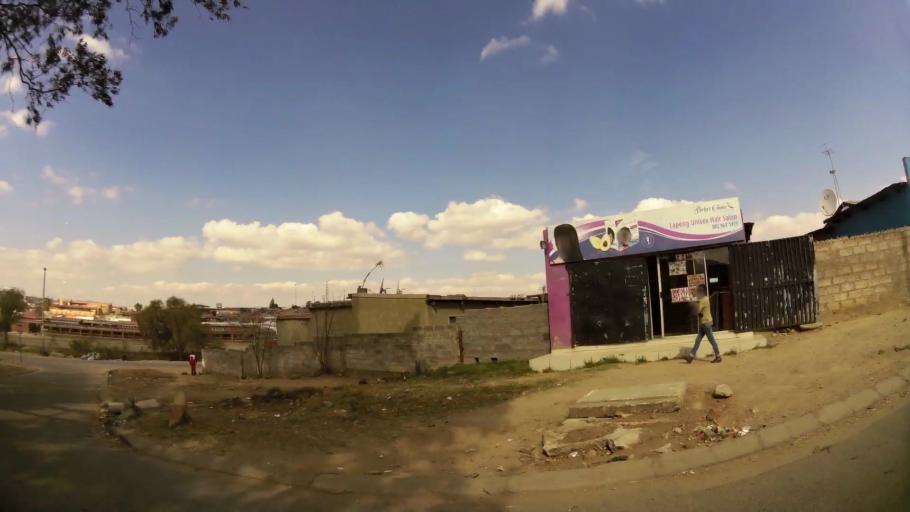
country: ZA
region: Gauteng
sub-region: Ekurhuleni Metropolitan Municipality
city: Tembisa
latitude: -26.0200
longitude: 28.1976
